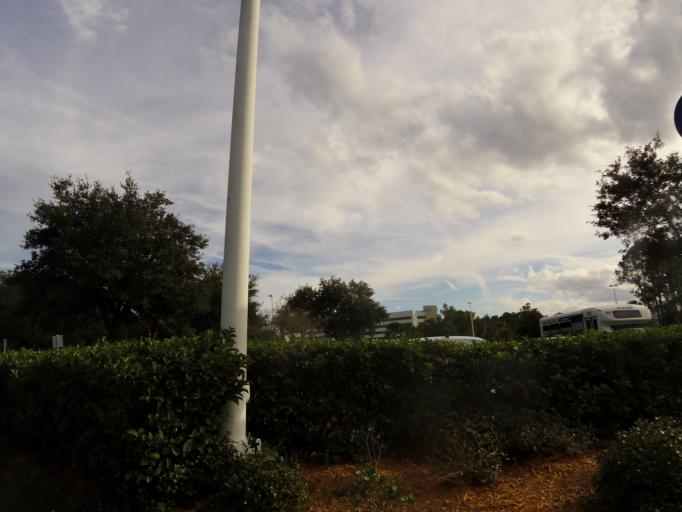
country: US
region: Florida
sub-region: Nassau County
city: Nassau Village-Ratliff
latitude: 30.4918
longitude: -81.6798
